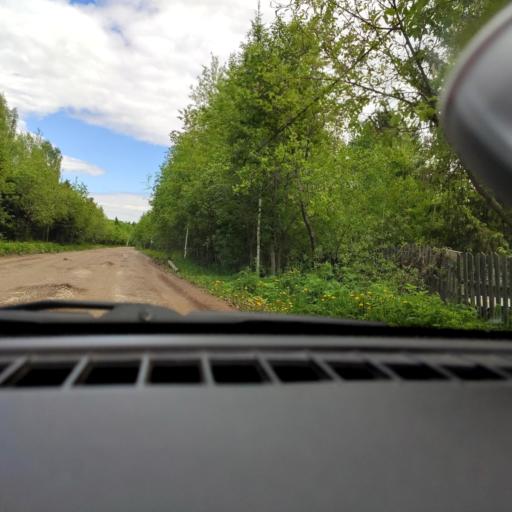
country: RU
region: Perm
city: Polazna
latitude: 58.2900
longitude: 56.1358
